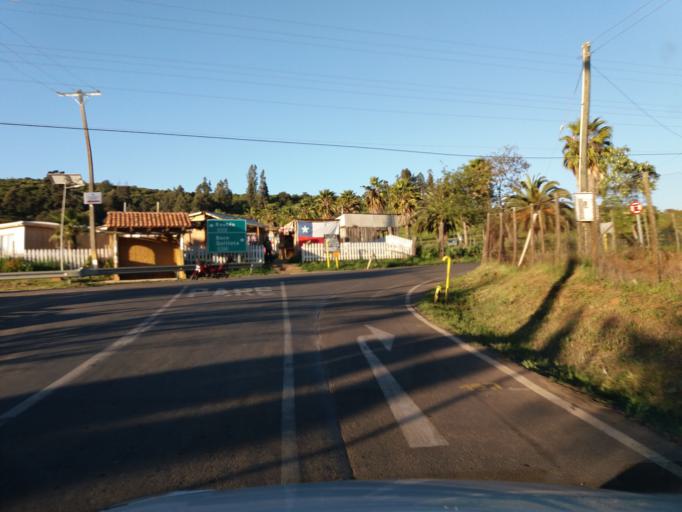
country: CL
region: Valparaiso
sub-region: Provincia de Quillota
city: Quillota
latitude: -32.8945
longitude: -71.2935
